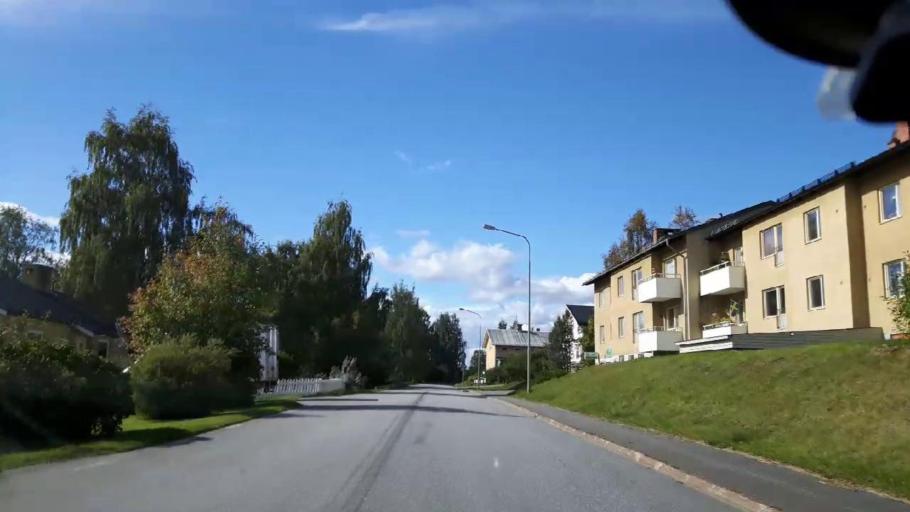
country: SE
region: Jaemtland
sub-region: Braecke Kommun
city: Braecke
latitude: 63.1691
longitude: 15.5795
